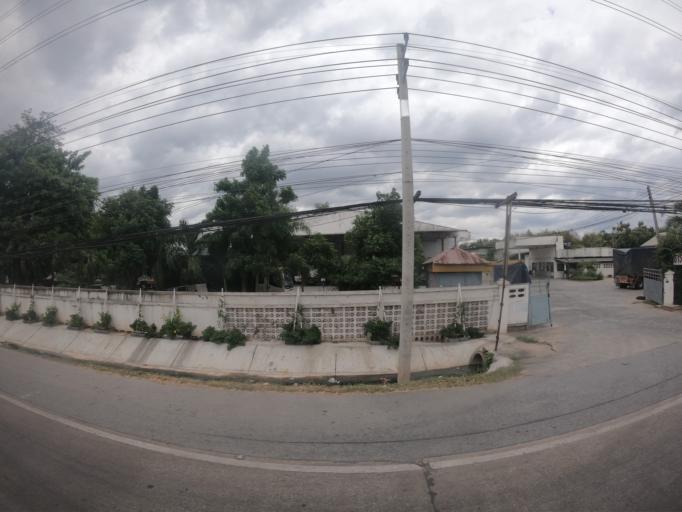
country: TH
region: Nakhon Ratchasima
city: Nakhon Ratchasima
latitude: 14.9193
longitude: 102.1464
